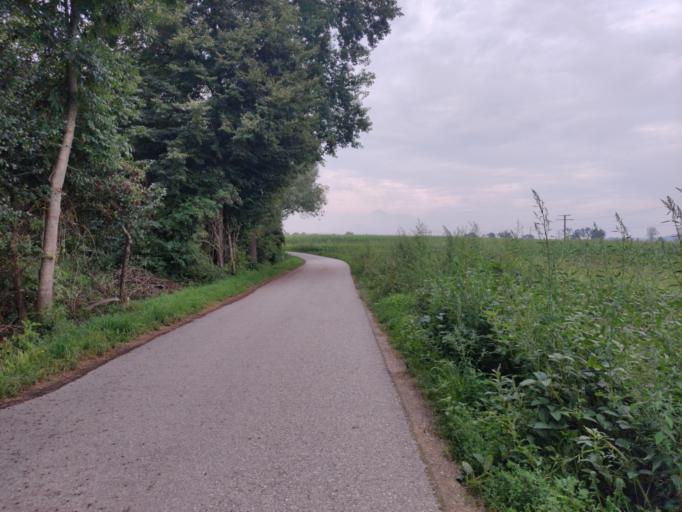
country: AT
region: Upper Austria
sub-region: Politischer Bezirk Linz-Land
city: Asten
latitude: 48.2336
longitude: 14.4282
